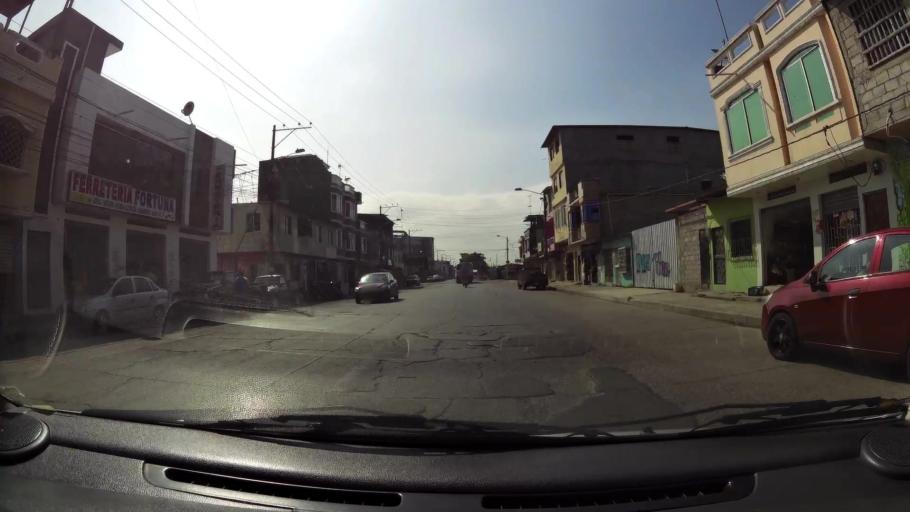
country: EC
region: Guayas
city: Eloy Alfaro
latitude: -2.1688
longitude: -79.7984
